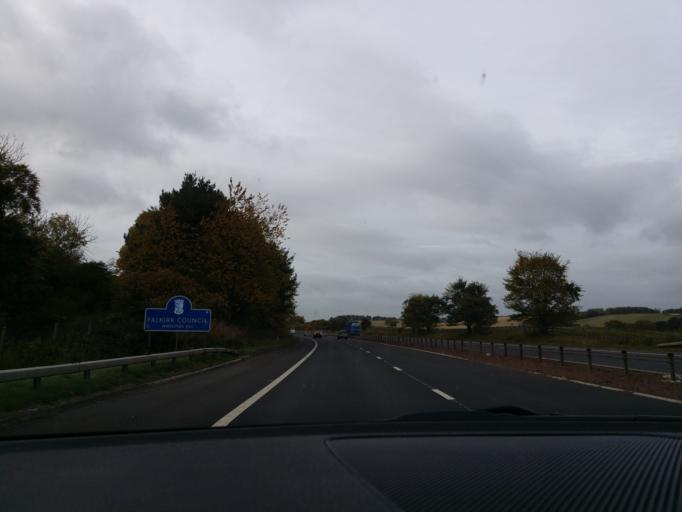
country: GB
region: Scotland
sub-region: West Lothian
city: Linlithgow
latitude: 55.9833
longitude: -3.6286
